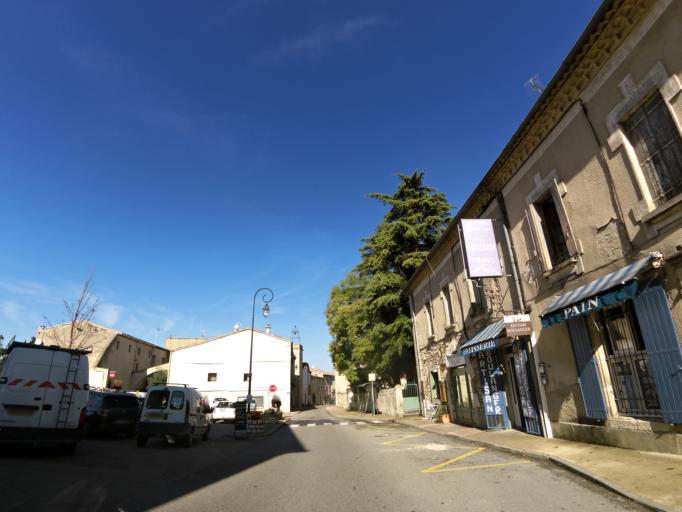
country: FR
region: Languedoc-Roussillon
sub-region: Departement du Gard
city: Ledignan
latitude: 43.9883
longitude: 4.1068
